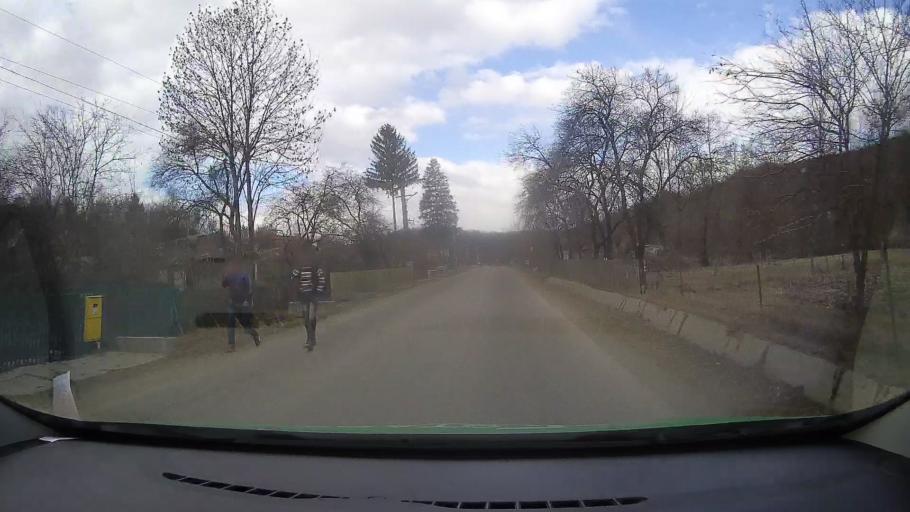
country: RO
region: Dambovita
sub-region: Comuna Valea Lunga
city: Valea Lunga-Cricov
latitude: 45.0644
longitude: 25.5587
